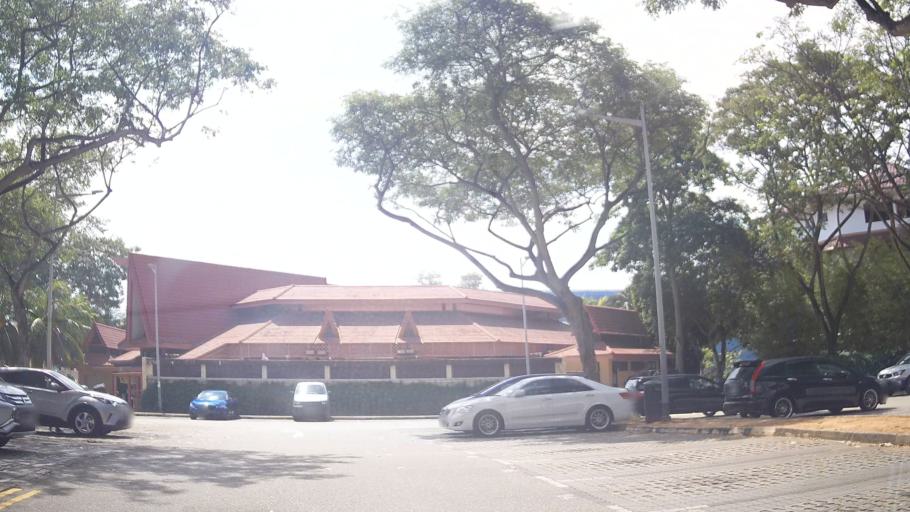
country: SG
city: Singapore
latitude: 1.3209
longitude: 103.9552
